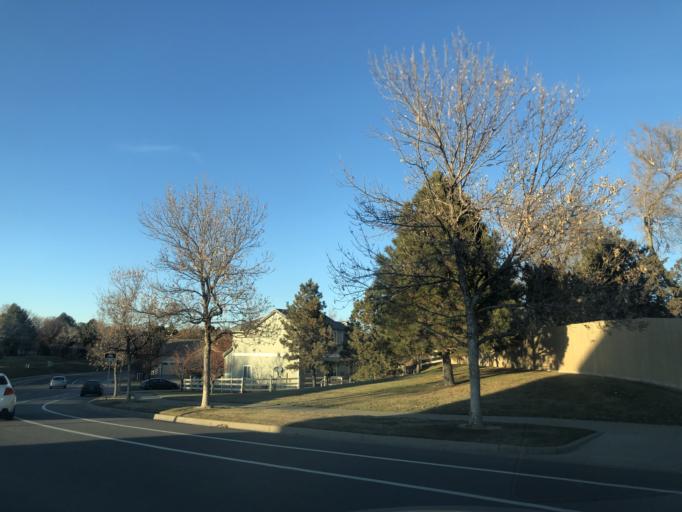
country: US
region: Colorado
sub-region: Adams County
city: Aurora
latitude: 39.7146
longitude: -104.8137
